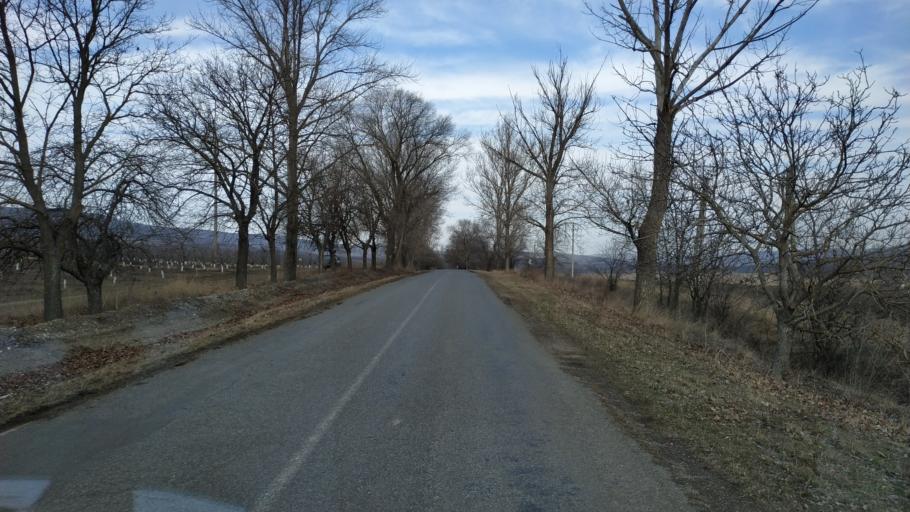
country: MD
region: Nisporeni
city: Nisporeni
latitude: 47.0989
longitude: 28.1302
